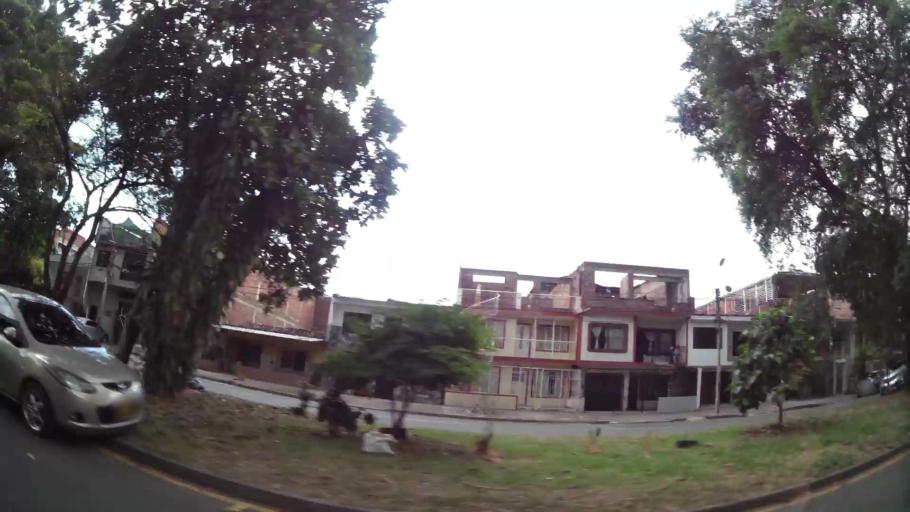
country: CO
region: Valle del Cauca
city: Cali
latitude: 3.4575
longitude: -76.4859
